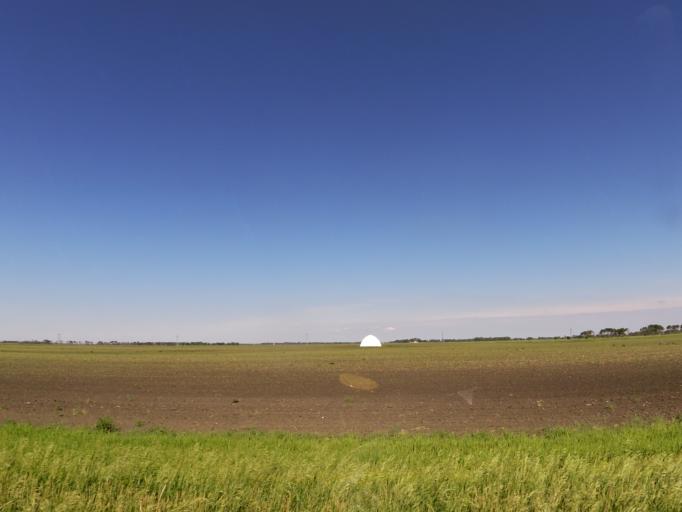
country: US
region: North Dakota
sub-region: Walsh County
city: Grafton
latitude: 48.3991
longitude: -97.2778
